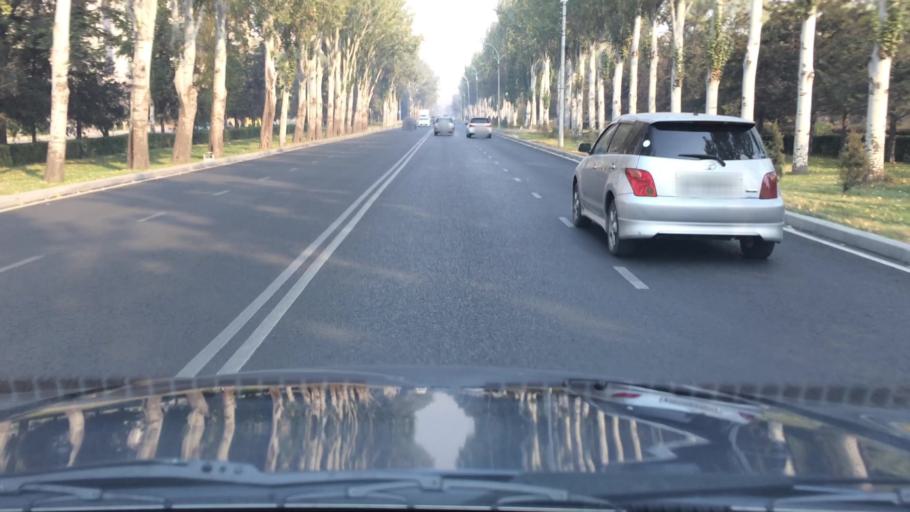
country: KG
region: Chuy
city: Bishkek
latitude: 42.8355
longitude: 74.5856
